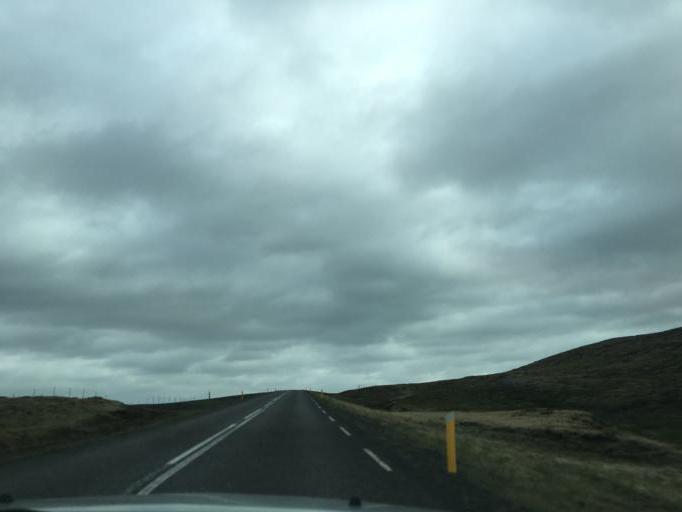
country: IS
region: South
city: Vestmannaeyjar
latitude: 64.2516
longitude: -20.2033
